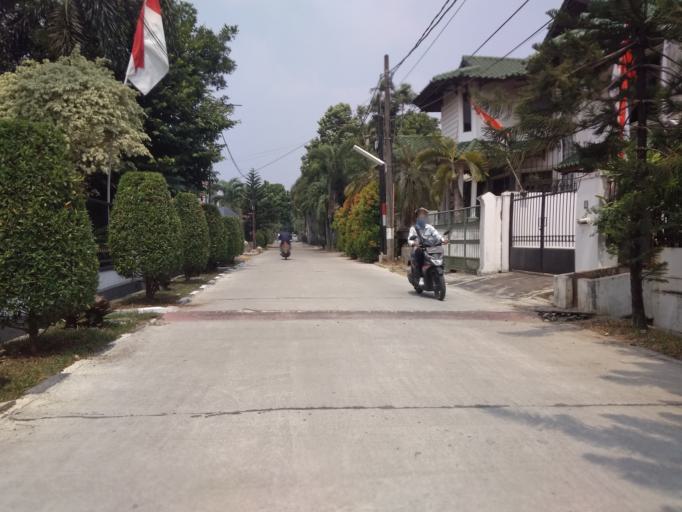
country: ID
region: West Java
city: Pamulang
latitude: -6.3198
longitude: 106.7905
